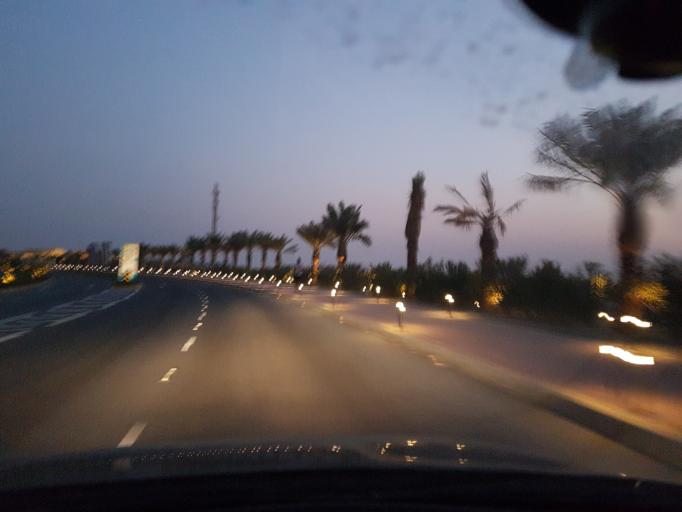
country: BH
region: Central Governorate
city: Dar Kulayb
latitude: 26.0181
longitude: 50.5088
